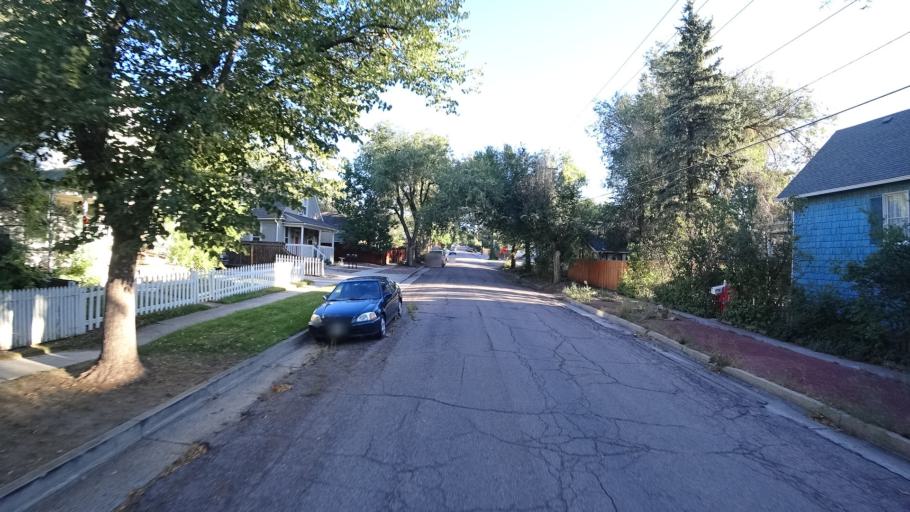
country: US
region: Colorado
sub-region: El Paso County
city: Colorado Springs
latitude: 38.8351
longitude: -104.8360
